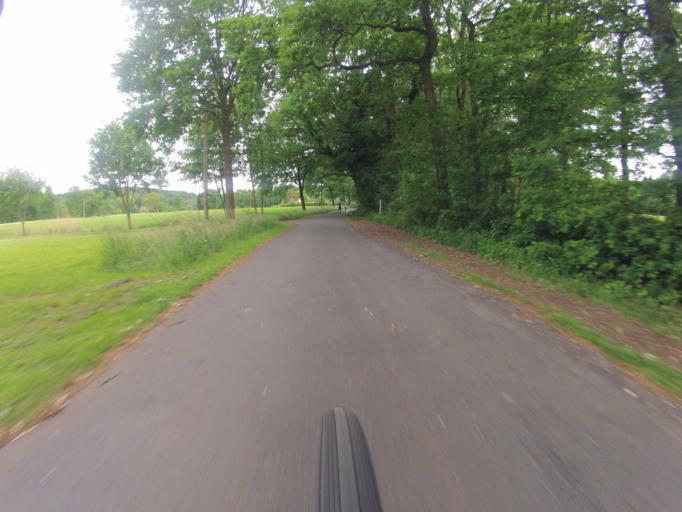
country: DE
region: North Rhine-Westphalia
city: Ibbenburen
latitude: 52.2480
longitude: 7.7472
